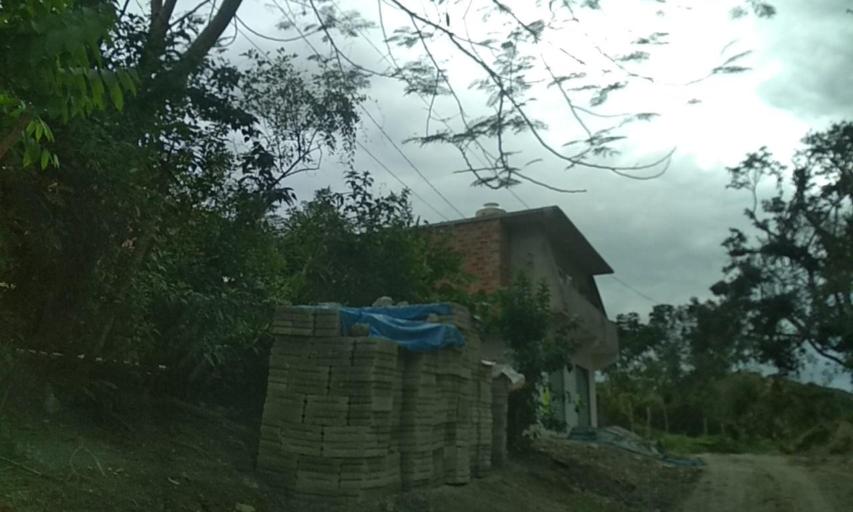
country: MX
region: Veracruz
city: Papantla de Olarte
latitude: 20.4591
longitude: -97.3152
